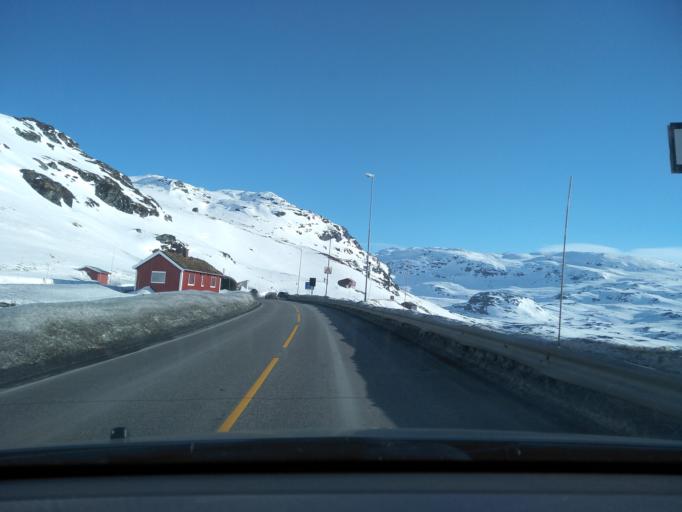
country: NO
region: Aust-Agder
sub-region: Bykle
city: Hovden
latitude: 59.8396
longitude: 6.9863
